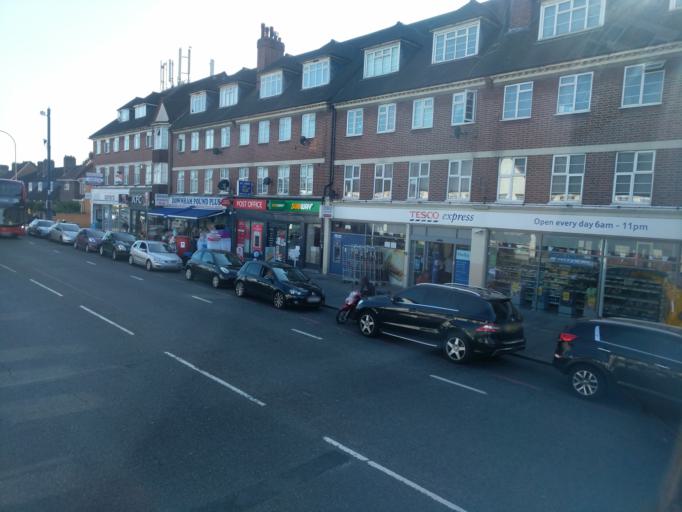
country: GB
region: England
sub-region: Greater London
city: Bromley
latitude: 51.4240
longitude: -0.0035
